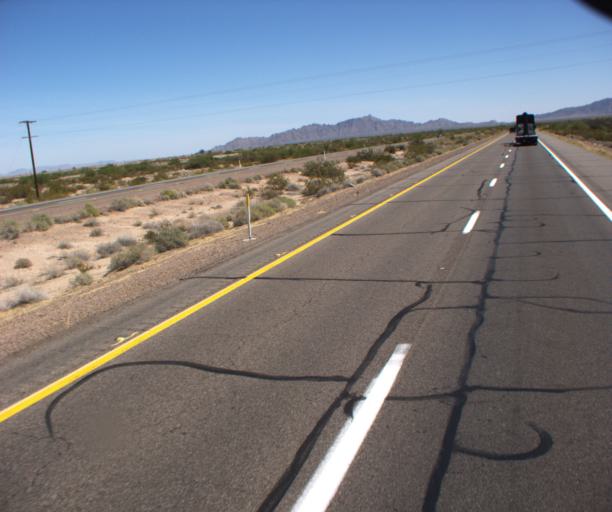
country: US
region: Arizona
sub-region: Yuma County
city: Wellton
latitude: 32.7025
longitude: -113.8934
